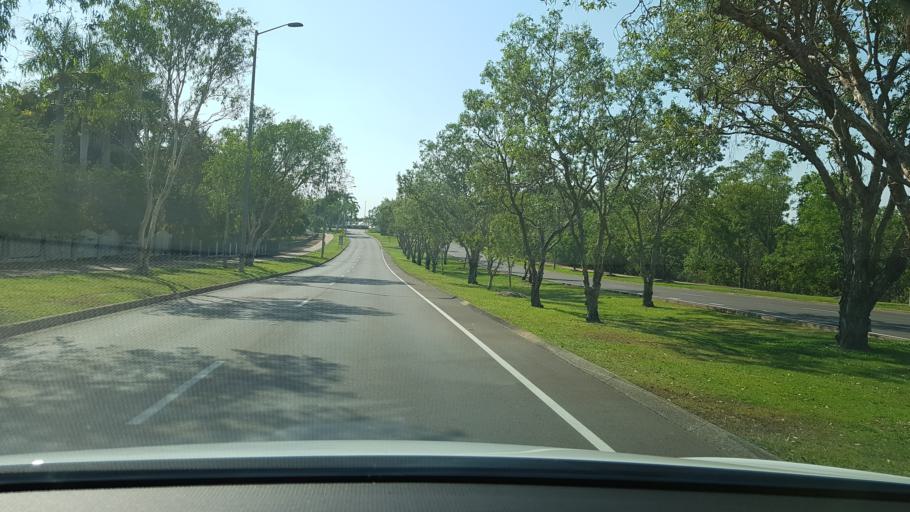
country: AU
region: Northern Territory
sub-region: Palmerston
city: Palmerston
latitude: -12.4855
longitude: 130.9878
